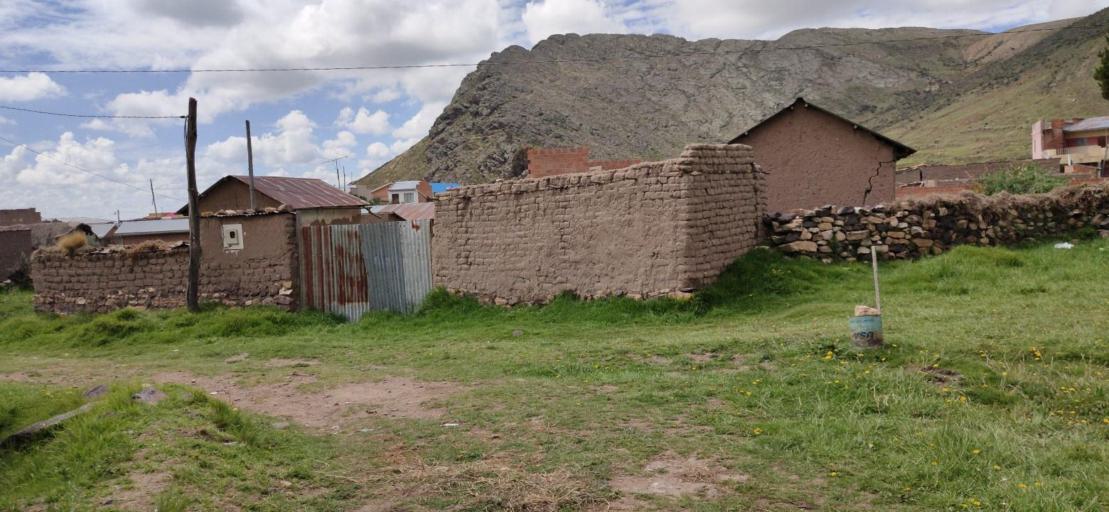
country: BO
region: La Paz
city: Batallas
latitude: -16.3473
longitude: -68.6367
